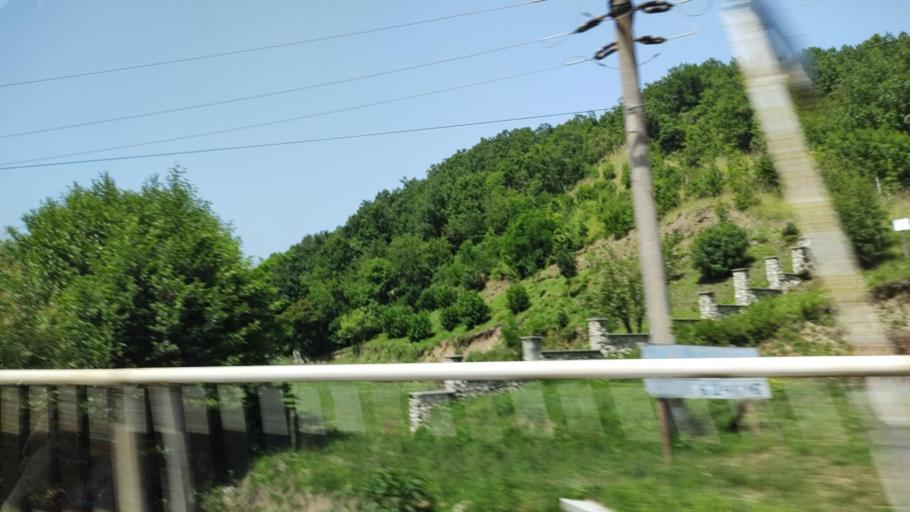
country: RO
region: Mehedinti
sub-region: Comuna Eselnita
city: Eselnita
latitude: 44.6848
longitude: 22.3466
